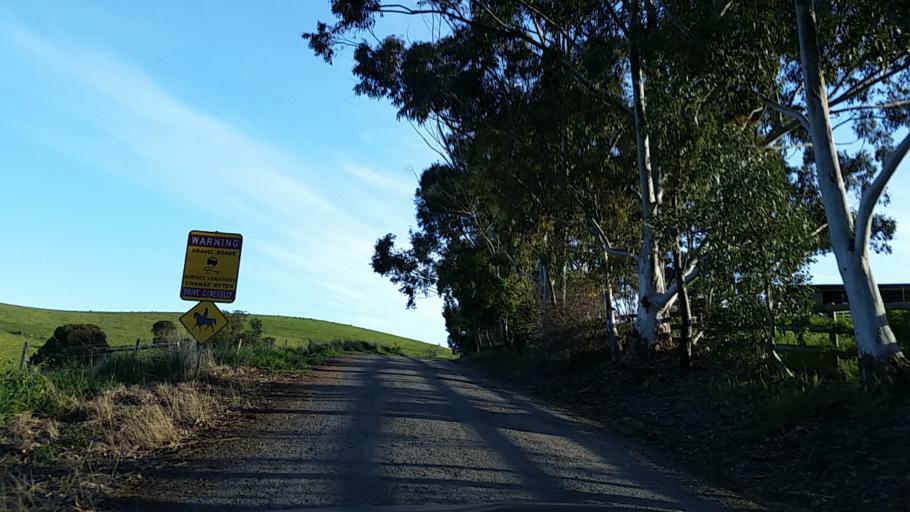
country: AU
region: South Australia
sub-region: Mount Barker
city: Meadows
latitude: -35.2399
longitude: 138.7617
